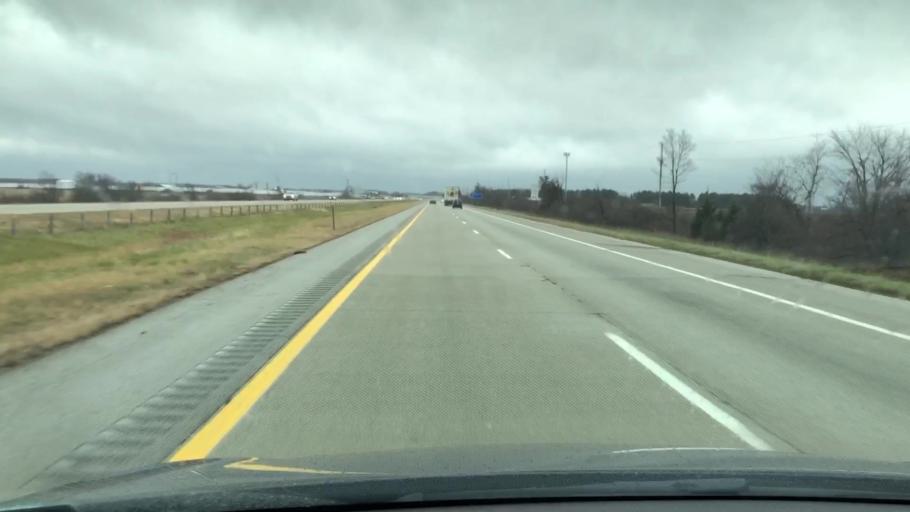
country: US
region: Ohio
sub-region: Lucas County
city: Sylvania
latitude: 41.7600
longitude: -83.6948
